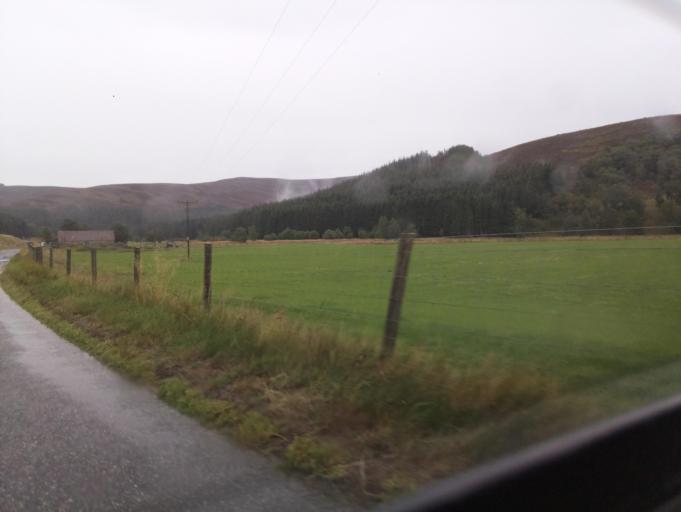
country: GB
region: Scotland
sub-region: Aberdeenshire
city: Ballater
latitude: 57.1629
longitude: -3.1825
